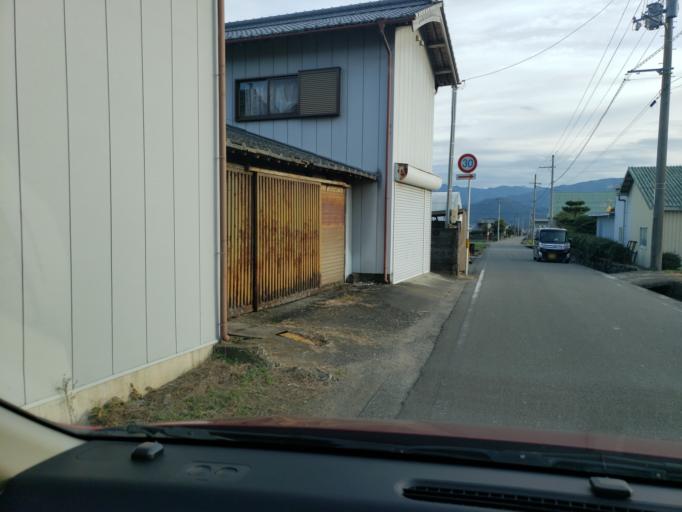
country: JP
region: Tokushima
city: Wakimachi
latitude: 34.0921
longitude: 134.2255
